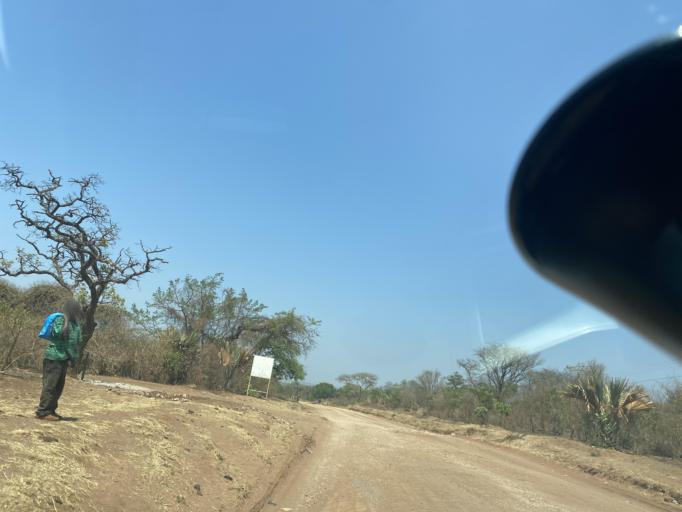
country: ZM
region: Lusaka
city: Lusaka
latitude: -15.5252
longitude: 28.1037
